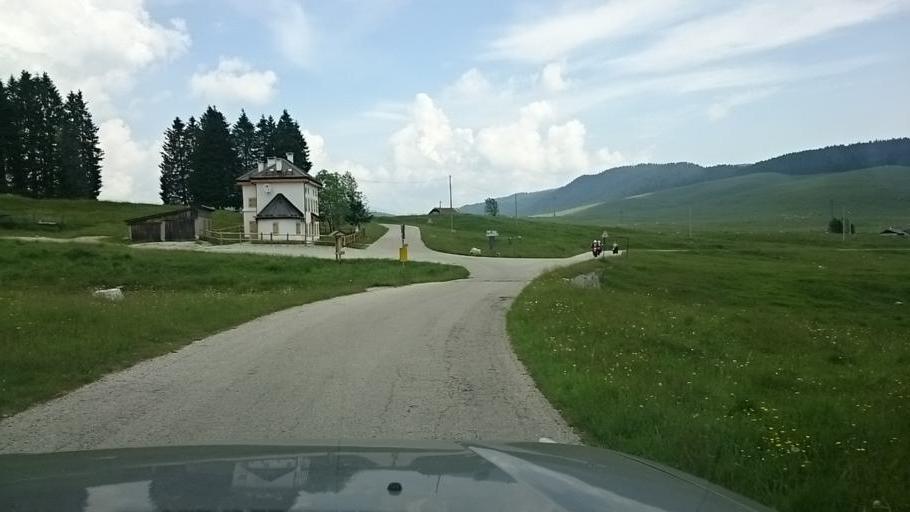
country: IT
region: Veneto
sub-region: Provincia di Vicenza
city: Foza
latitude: 45.9465
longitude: 11.6086
